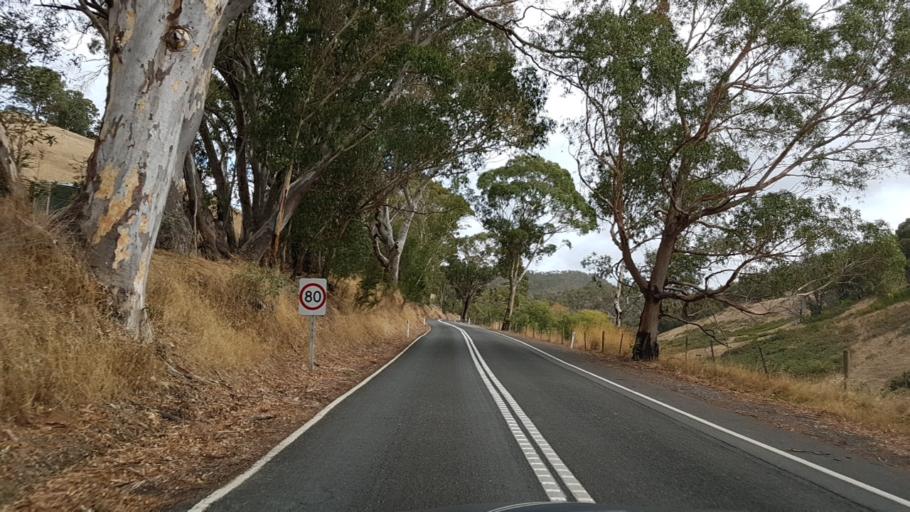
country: AU
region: South Australia
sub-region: Adelaide Hills
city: Gumeracha
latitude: -34.8312
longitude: 138.8491
